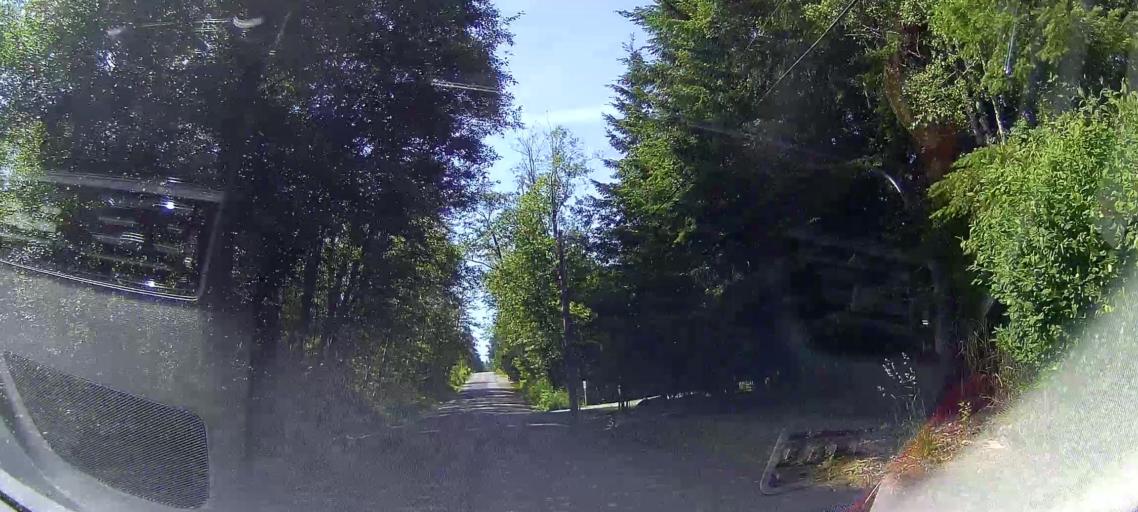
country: US
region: Washington
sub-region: Skagit County
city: Sedro-Woolley
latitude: 48.5493
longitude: -122.2476
